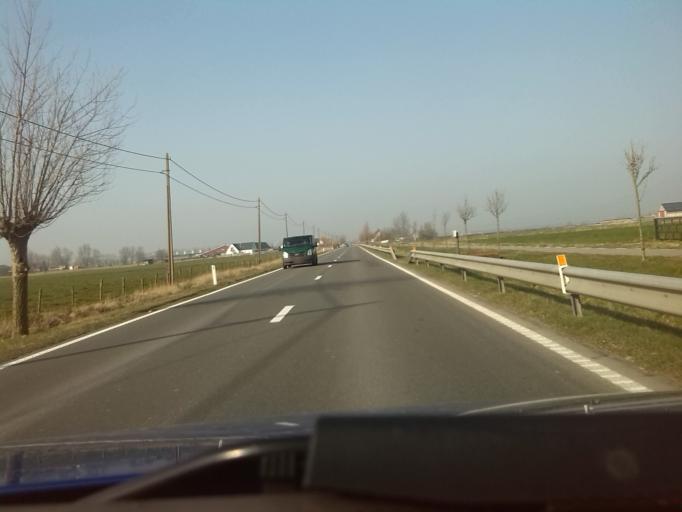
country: BE
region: Flanders
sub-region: Provincie West-Vlaanderen
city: Wenduine
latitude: 51.2834
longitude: 3.0892
